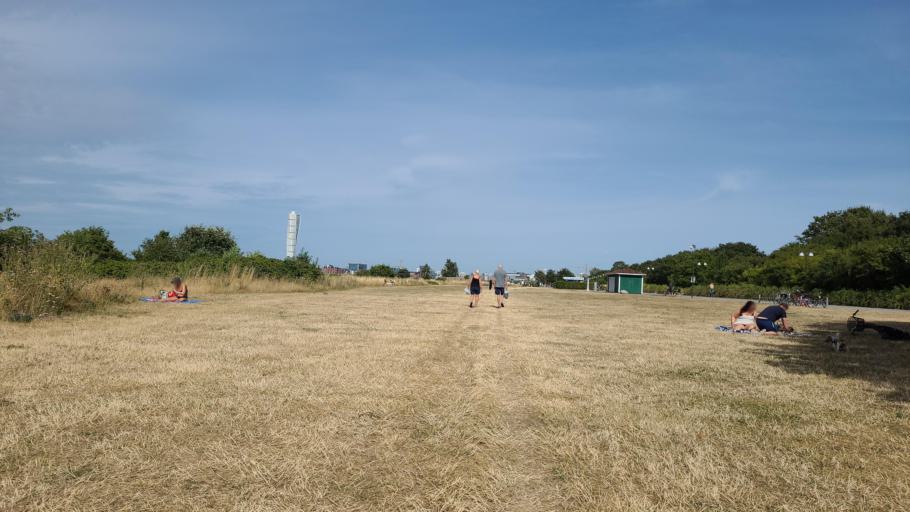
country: SE
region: Skane
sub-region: Malmo
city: Malmoe
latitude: 55.5983
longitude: 12.9534
